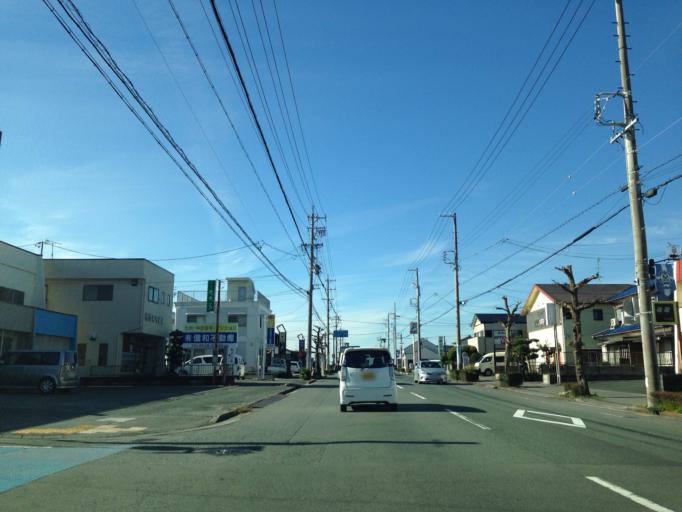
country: JP
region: Shizuoka
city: Iwata
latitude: 34.7185
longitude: 137.8672
